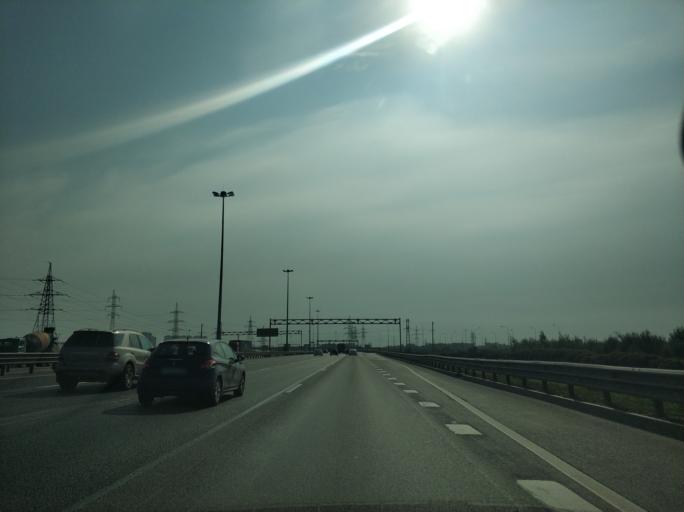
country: RU
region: Leningrad
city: Murino
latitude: 60.0230
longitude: 30.4526
